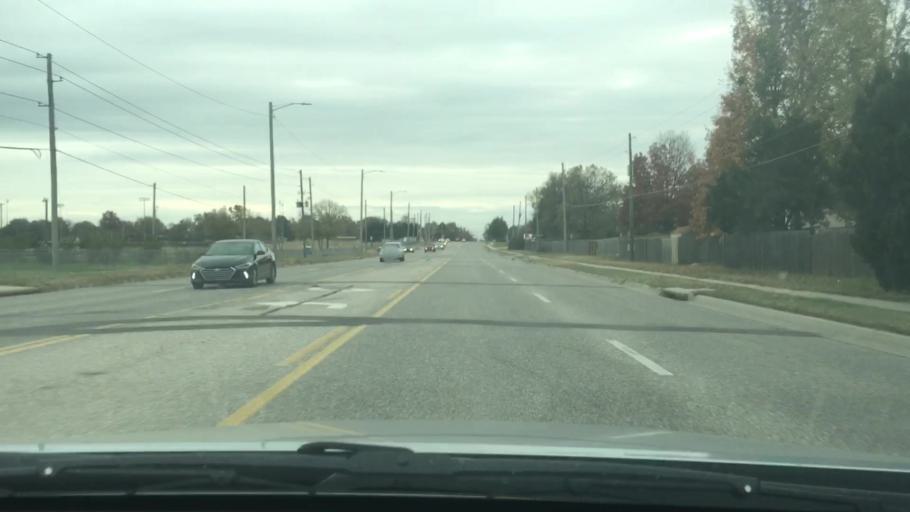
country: US
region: Kansas
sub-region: Sedgwick County
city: Maize
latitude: 37.7135
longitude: -97.4261
